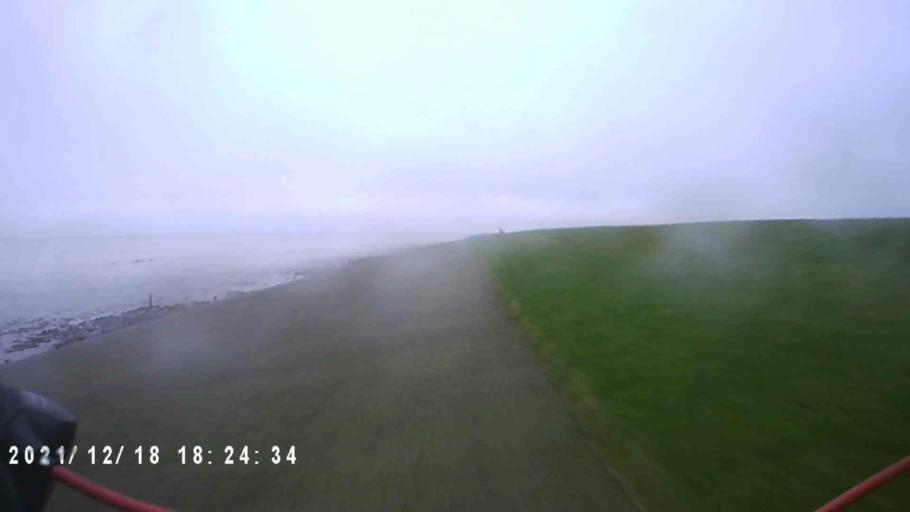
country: NL
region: Friesland
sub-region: Gemeente Dongeradeel
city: Ternaard
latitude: 53.3987
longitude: 5.9952
